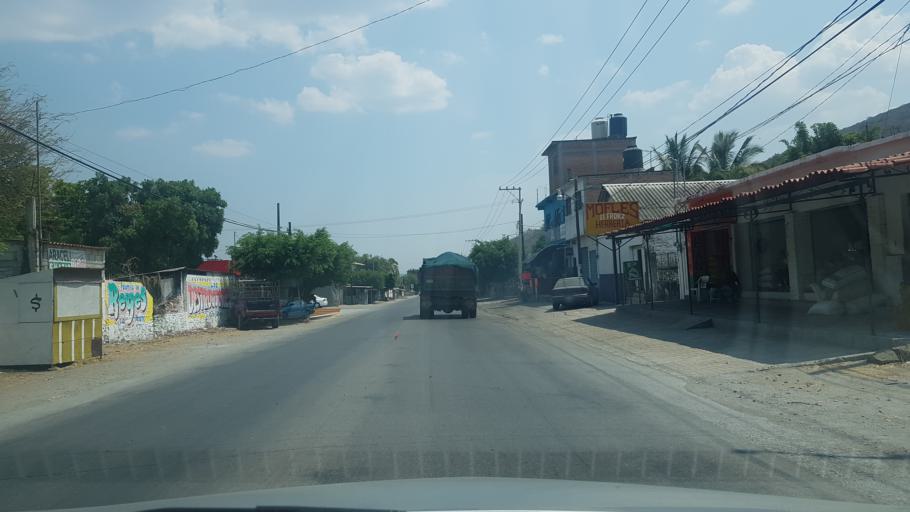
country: MX
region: Morelos
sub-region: Tlaltizapan de Zapata
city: Colonia Palo Prieto (Chipitongo)
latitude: 18.7185
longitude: -99.1202
